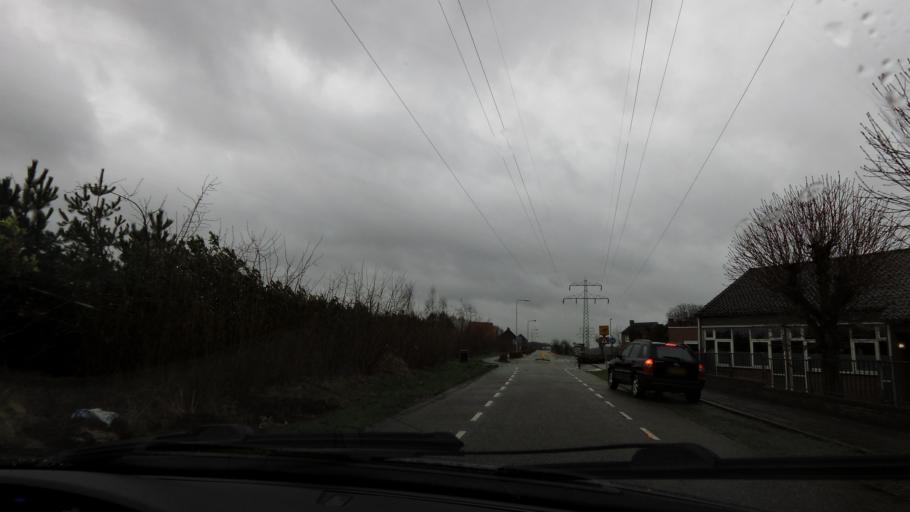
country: NL
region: Limburg
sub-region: Gemeente Sittard-Geleen
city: Limbricht
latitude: 51.0135
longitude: 5.8218
